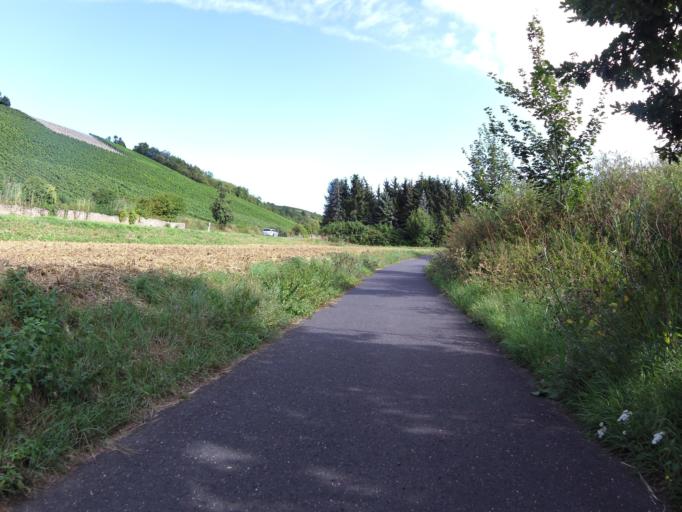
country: DE
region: Bavaria
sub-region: Regierungsbezirk Unterfranken
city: Mainstockheim
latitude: 49.7907
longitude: 10.1525
